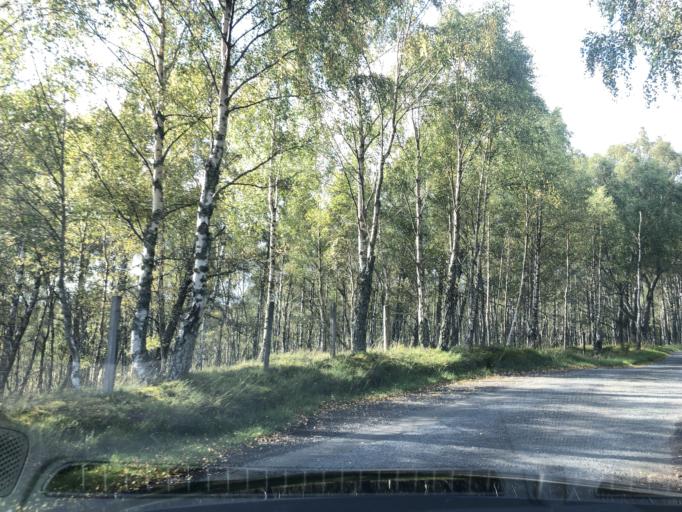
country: GB
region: Scotland
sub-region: Highland
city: Aviemore
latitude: 57.0634
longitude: -3.8975
